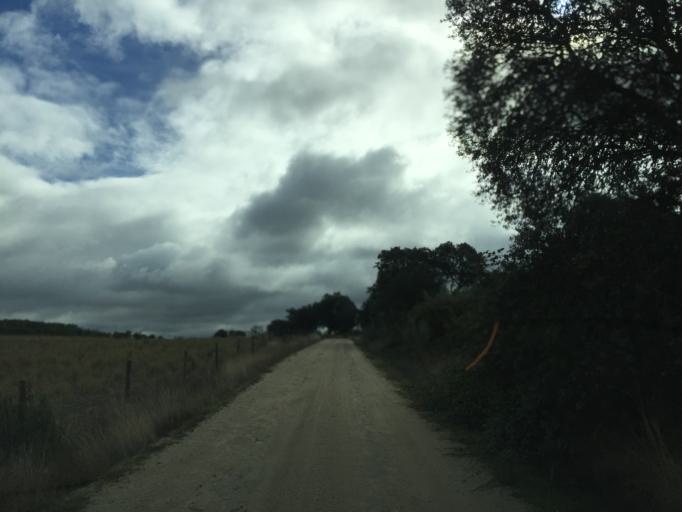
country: PT
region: Portalegre
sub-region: Alter do Chao
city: Alter do Chao
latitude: 39.2384
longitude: -7.6973
